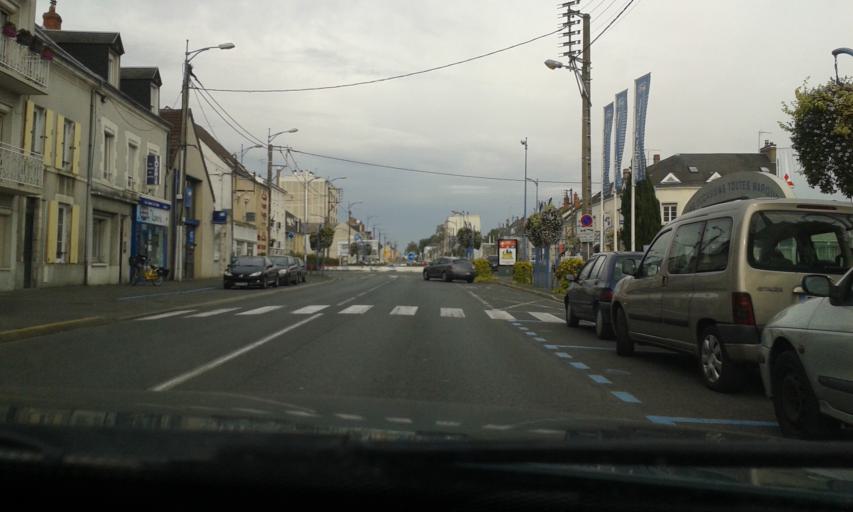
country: FR
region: Centre
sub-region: Departement du Loiret
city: Fleury-les-Aubrais
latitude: 47.9335
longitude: 1.8949
